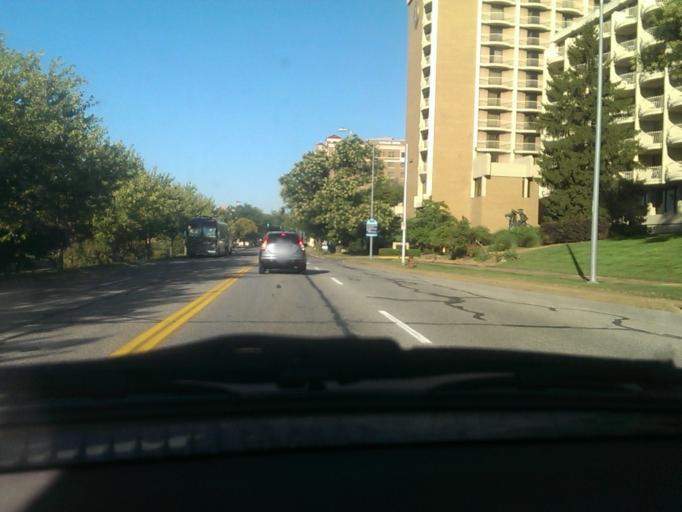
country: US
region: Kansas
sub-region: Johnson County
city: Westwood
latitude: 39.0394
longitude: -94.5939
